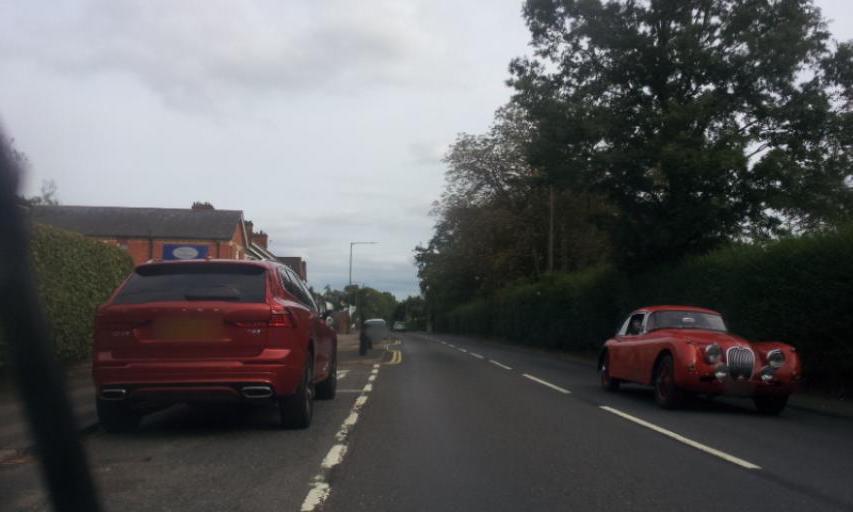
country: GB
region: England
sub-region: Kent
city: Tonbridge
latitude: 51.2161
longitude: 0.2422
